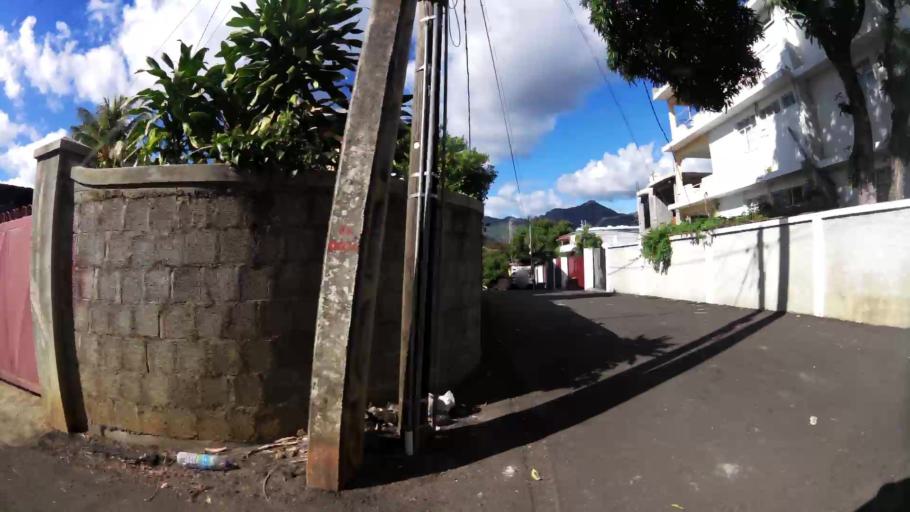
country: MU
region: Pamplemousses
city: Le Hochet
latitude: -20.1489
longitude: 57.5128
